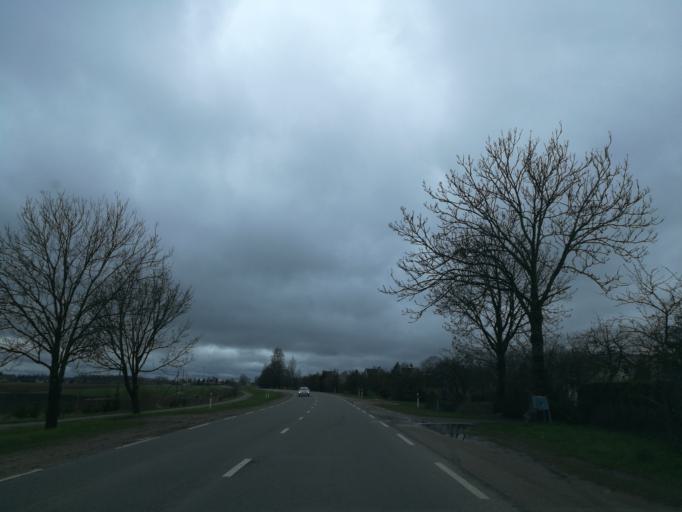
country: LT
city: Raseiniai
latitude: 55.4000
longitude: 23.1481
